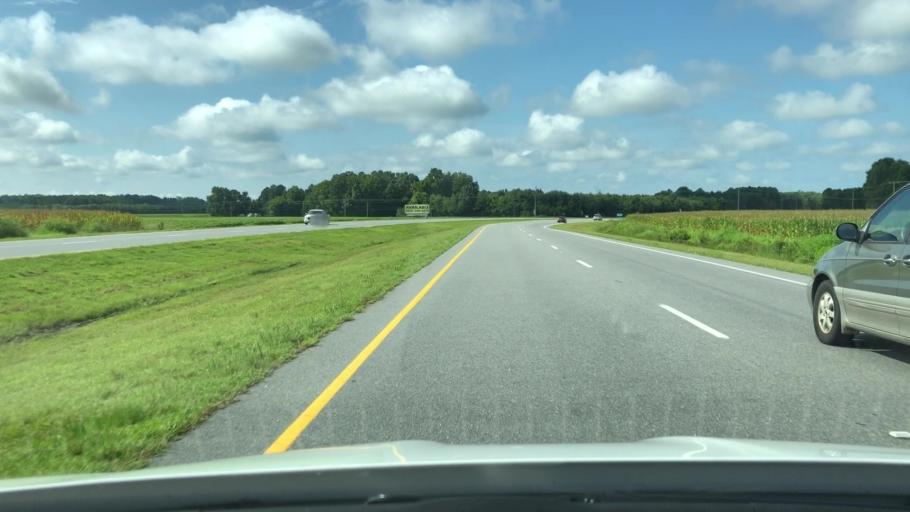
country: US
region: North Carolina
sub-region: Perquimans County
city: Hertford
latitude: 36.1357
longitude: -76.4920
